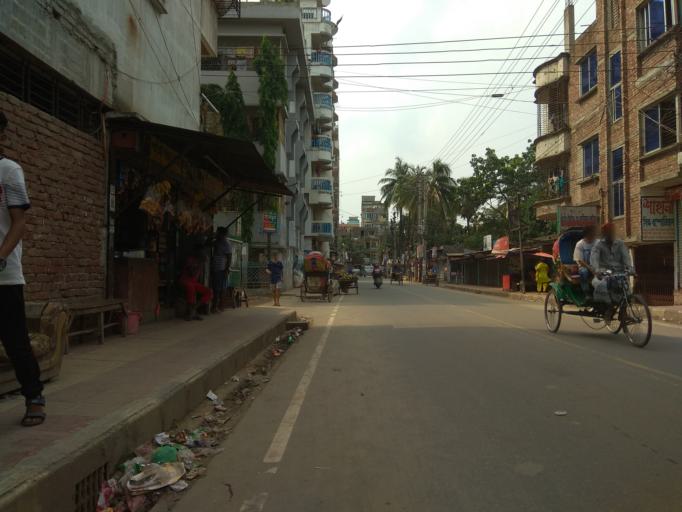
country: BD
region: Dhaka
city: Tungi
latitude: 23.8165
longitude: 90.3726
